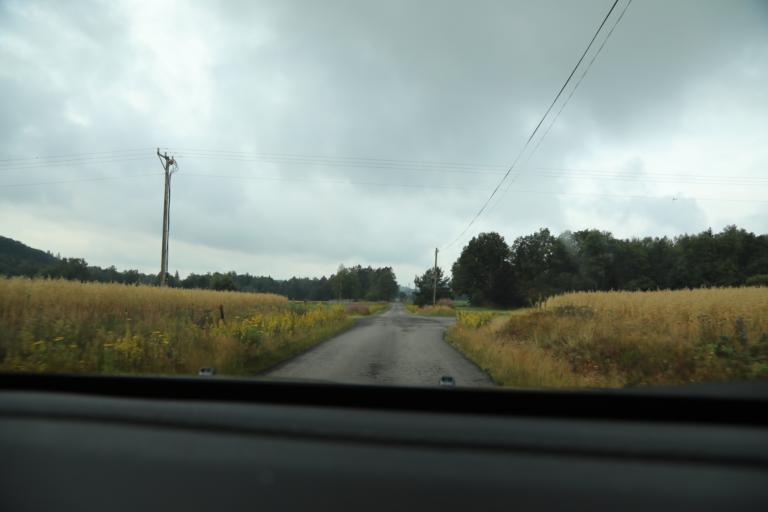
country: SE
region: Halland
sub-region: Falkenbergs Kommun
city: Falkenberg
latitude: 57.1163
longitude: 12.6885
